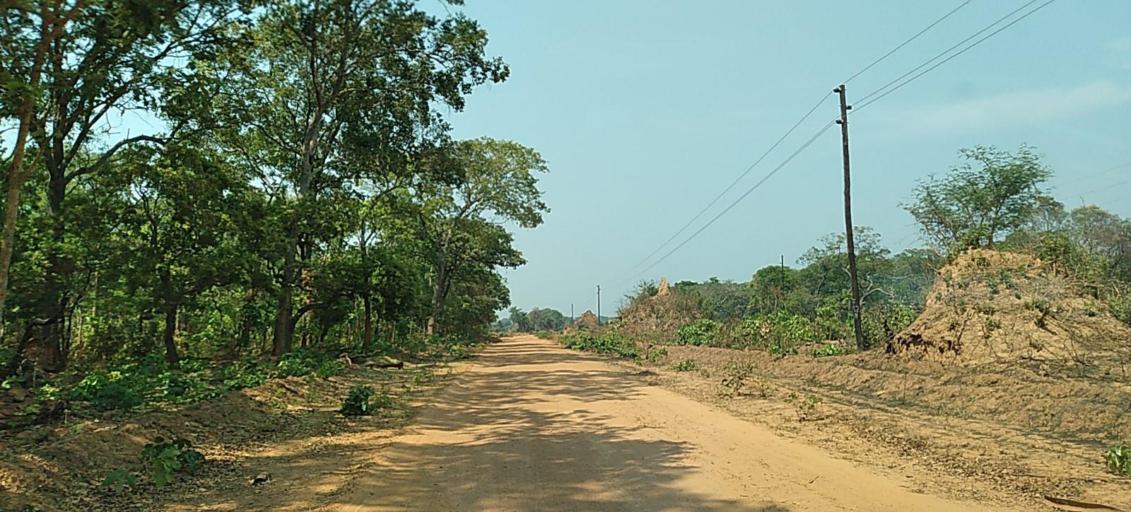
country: ZM
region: Copperbelt
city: Chingola
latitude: -13.0565
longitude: 27.4244
